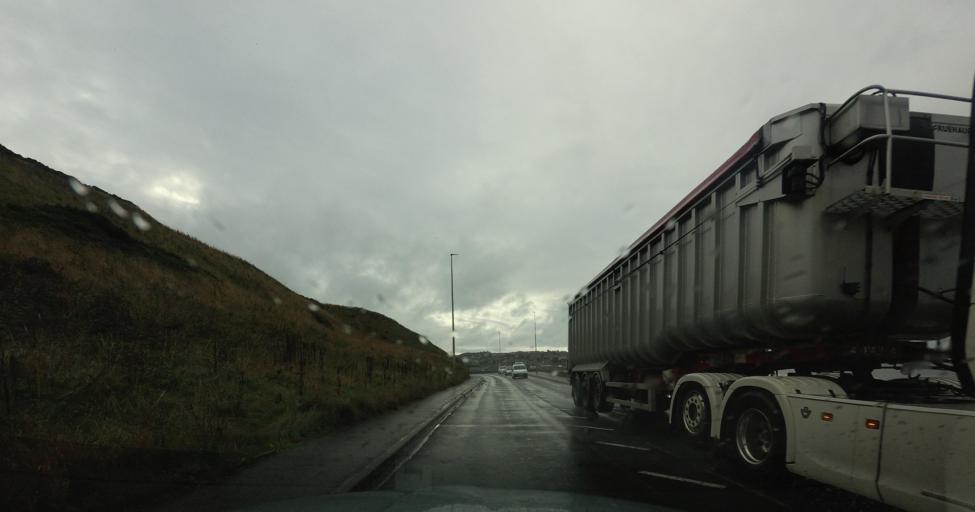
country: GB
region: Scotland
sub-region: Aberdeenshire
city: Macduff
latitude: 57.6660
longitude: -2.5074
